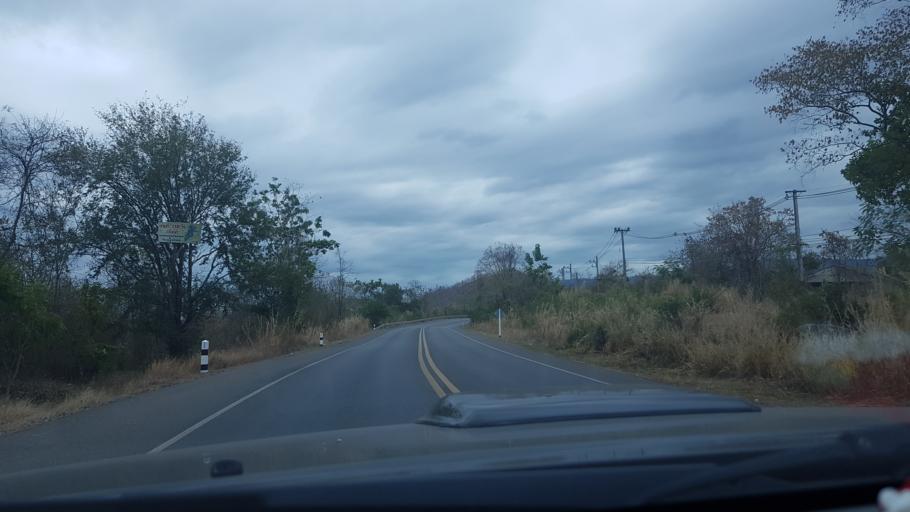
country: TH
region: Phetchabun
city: Phetchabun
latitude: 16.5358
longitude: 101.1135
